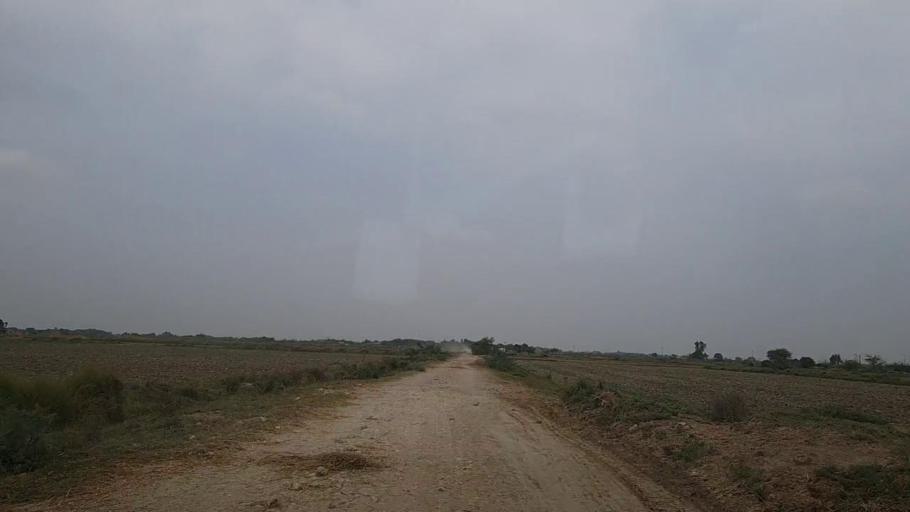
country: PK
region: Sindh
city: Mirpur Sakro
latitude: 24.5972
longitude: 67.6972
